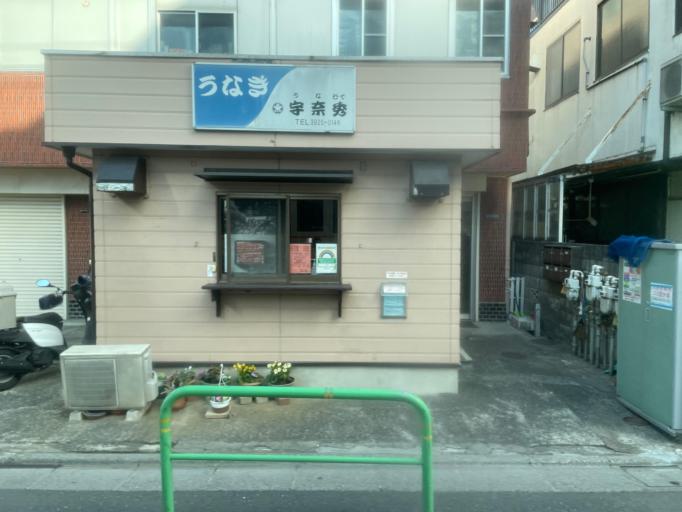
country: JP
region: Tokyo
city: Musashino
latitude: 35.7427
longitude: 139.5870
